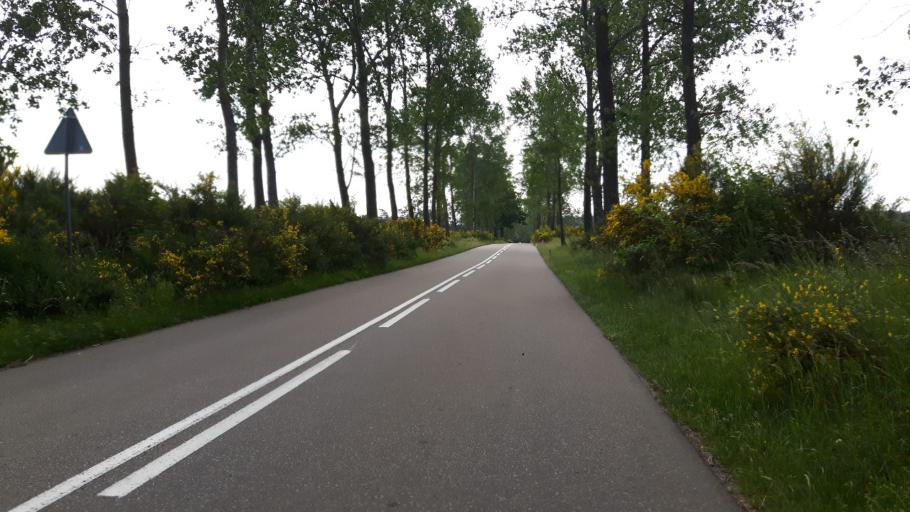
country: PL
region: Pomeranian Voivodeship
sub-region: Powiat leborski
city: Leba
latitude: 54.7480
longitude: 17.7115
